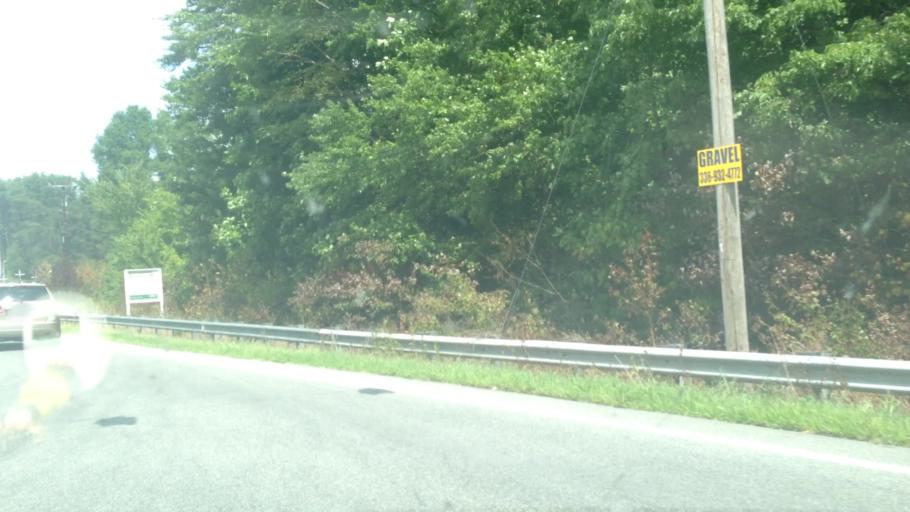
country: US
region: North Carolina
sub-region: Guilford County
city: Stokesdale
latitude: 36.2455
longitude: -79.9728
